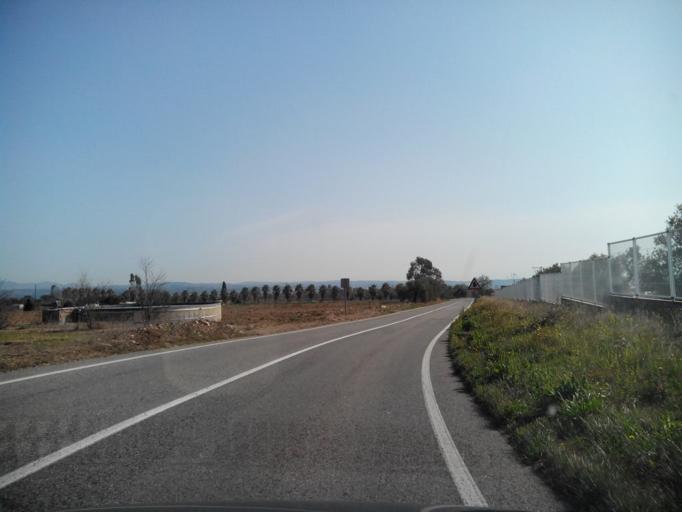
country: ES
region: Catalonia
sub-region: Provincia de Tarragona
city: La Selva
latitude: 41.2132
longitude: 1.1598
